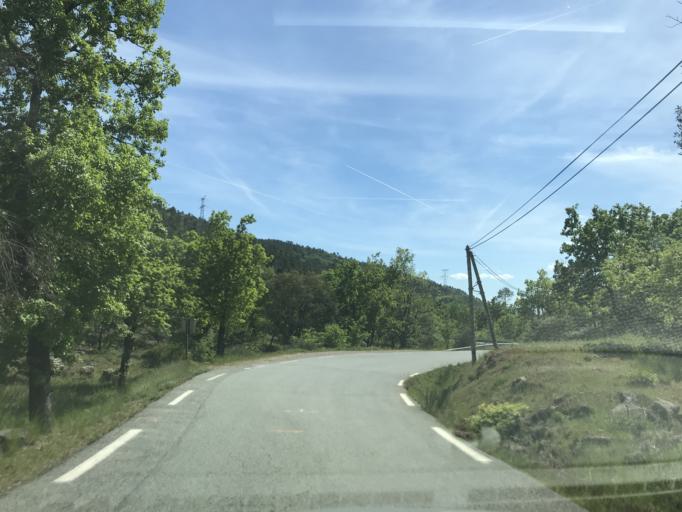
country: FR
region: Provence-Alpes-Cote d'Azur
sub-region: Departement du Var
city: Montauroux
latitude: 43.5830
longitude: 6.8120
